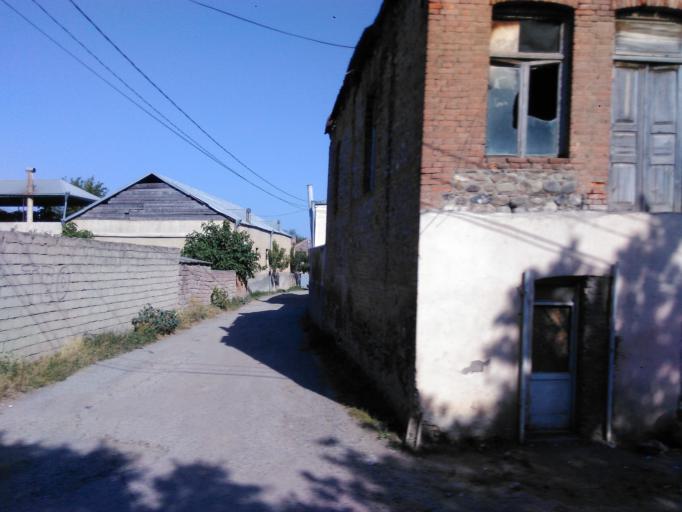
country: GE
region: Shida Kartli
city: Kaspi
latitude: 41.9334
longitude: 44.5761
